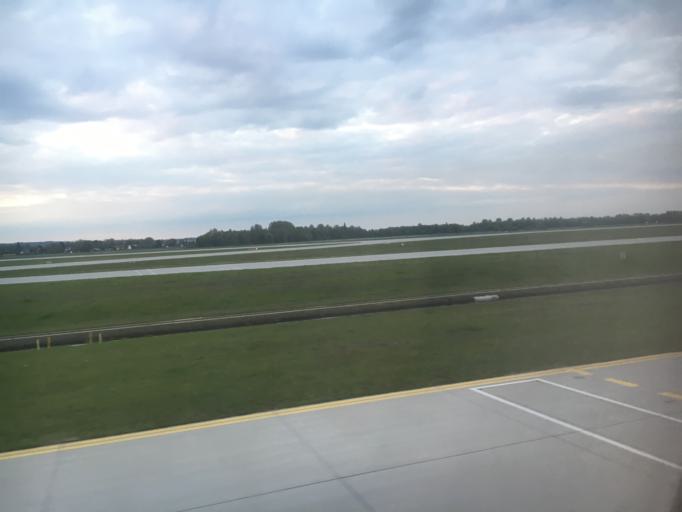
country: DE
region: Bavaria
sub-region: Upper Bavaria
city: Hallbergmoos
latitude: 48.3599
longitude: 11.7789
